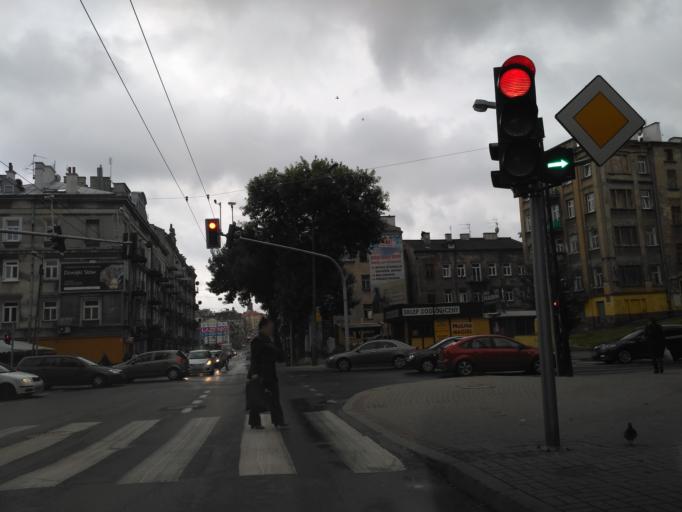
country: PL
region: Lublin Voivodeship
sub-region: Powiat lubelski
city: Lublin
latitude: 51.2538
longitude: 22.5692
